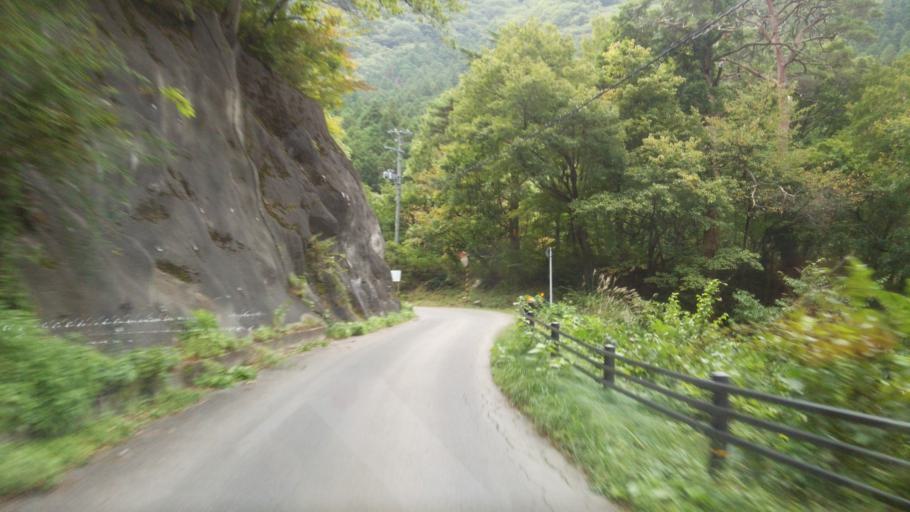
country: JP
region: Fukushima
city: Inawashiro
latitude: 37.3810
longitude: 139.9404
